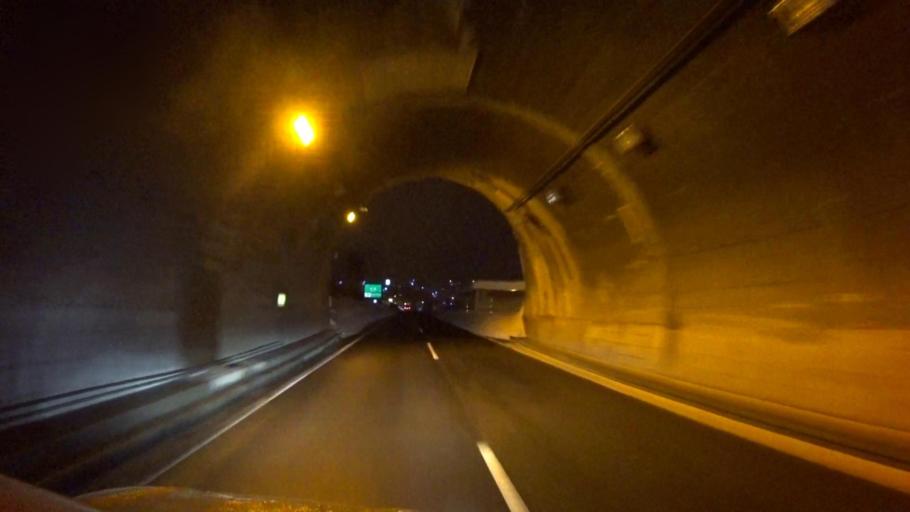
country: JP
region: Hokkaido
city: Otaru
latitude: 43.1740
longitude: 141.0304
